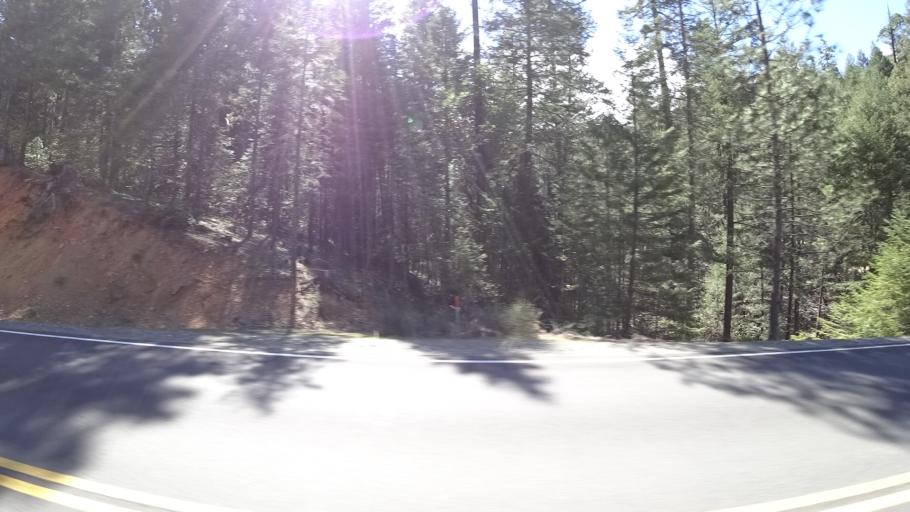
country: US
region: California
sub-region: Trinity County
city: Lewiston
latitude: 40.8908
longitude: -122.7956
